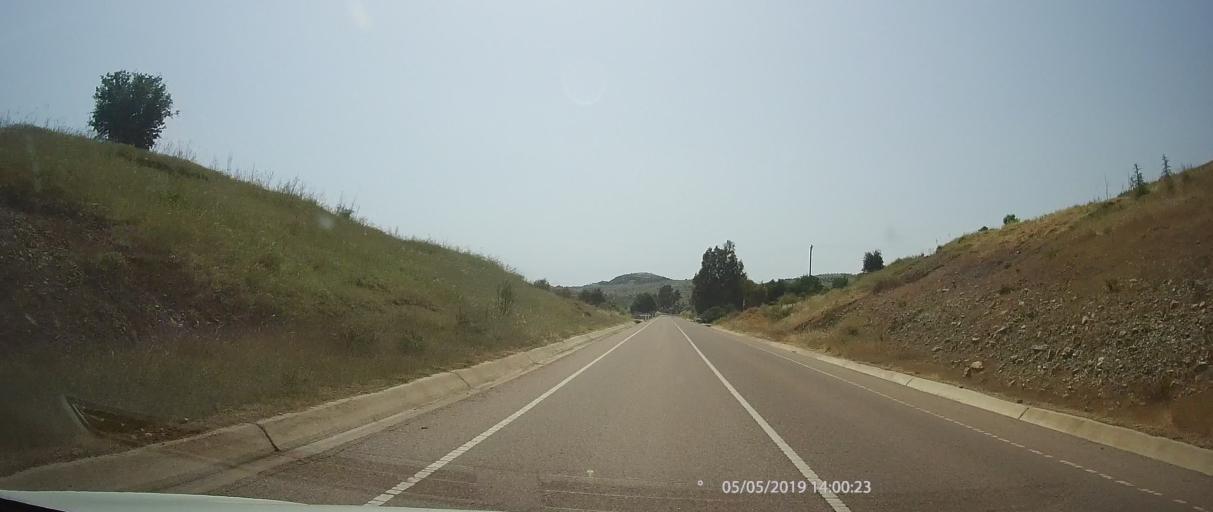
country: CY
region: Limassol
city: Pissouri
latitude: 34.7784
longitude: 32.6606
